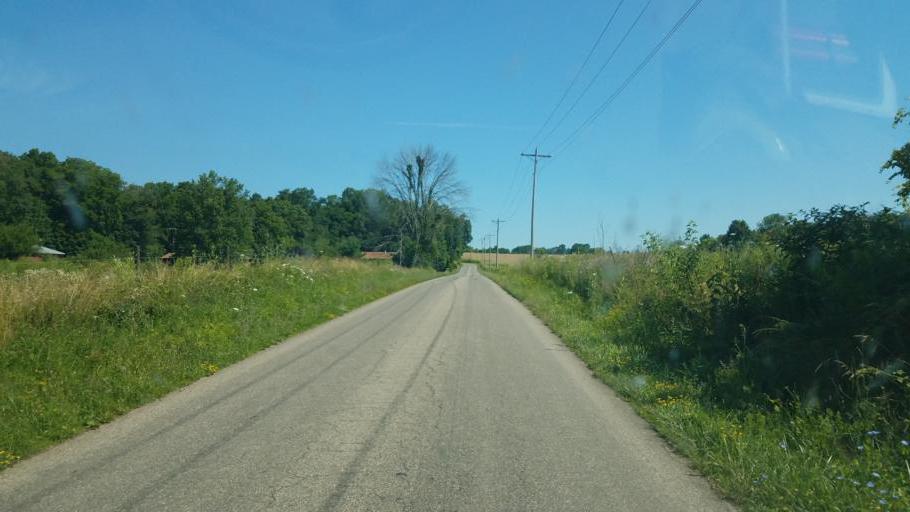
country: US
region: Ohio
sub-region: Knox County
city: Fredericktown
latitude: 40.4856
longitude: -82.6265
